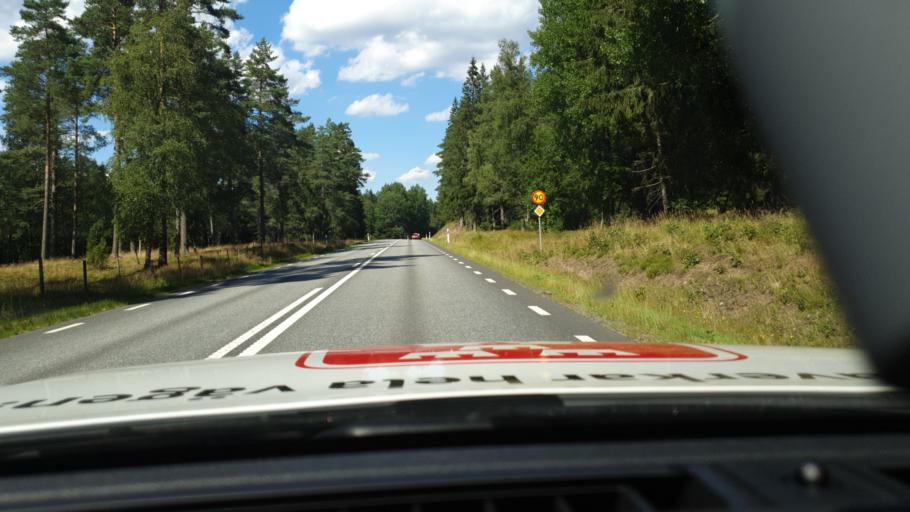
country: SE
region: Joenkoeping
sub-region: Vaggeryds Kommun
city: Vaggeryd
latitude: 57.4584
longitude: 14.3153
